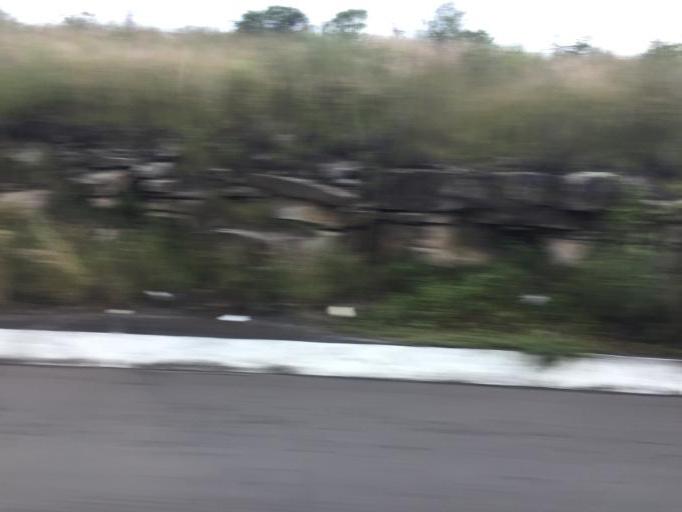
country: MX
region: Mexico
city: Huaniqueo de Morales
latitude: 19.8830
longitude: -101.4949
